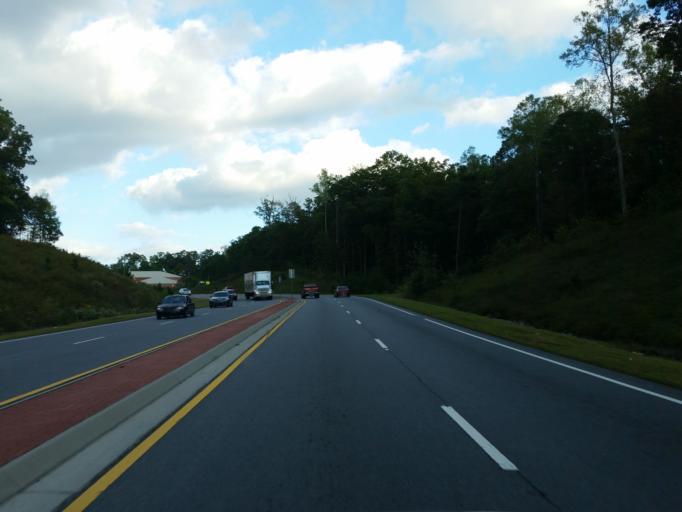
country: US
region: Georgia
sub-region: Cobb County
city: Fair Oaks
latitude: 33.8954
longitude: -84.5847
